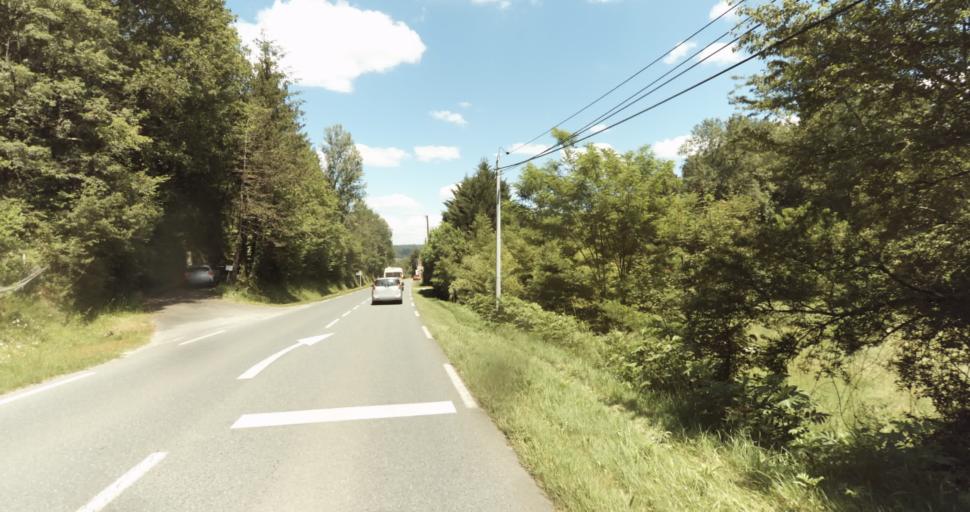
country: FR
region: Aquitaine
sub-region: Departement de la Dordogne
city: Le Bugue
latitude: 44.8441
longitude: 0.8933
